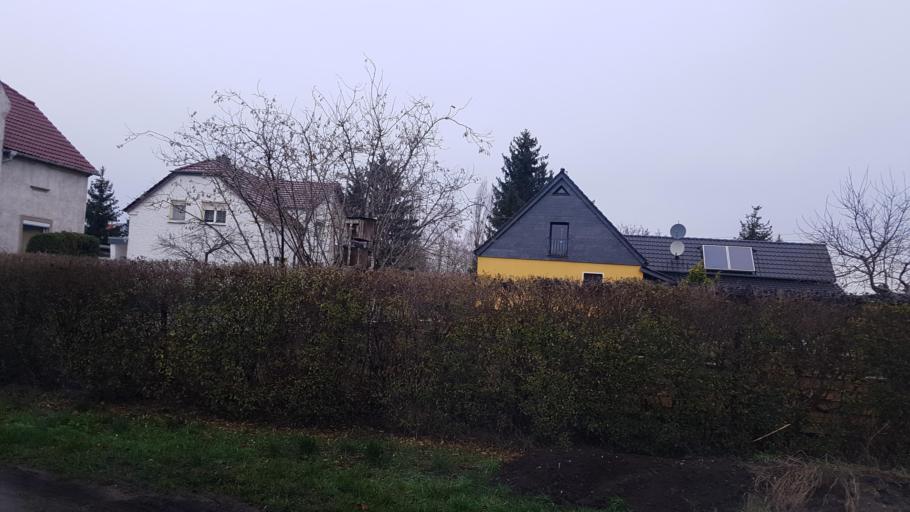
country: DE
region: Brandenburg
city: Lauchhammer
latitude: 51.4692
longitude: 13.7838
